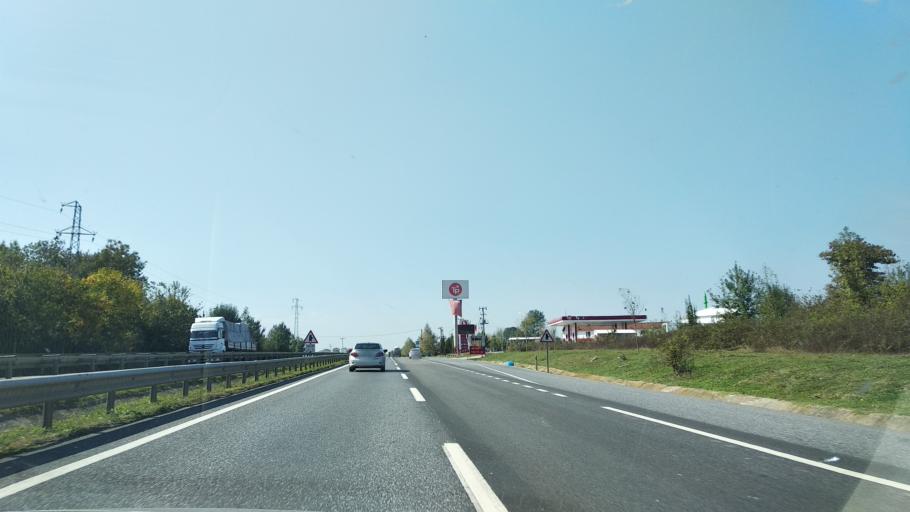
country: TR
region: Kocaeli
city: Derbent
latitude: 40.7313
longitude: 30.1614
